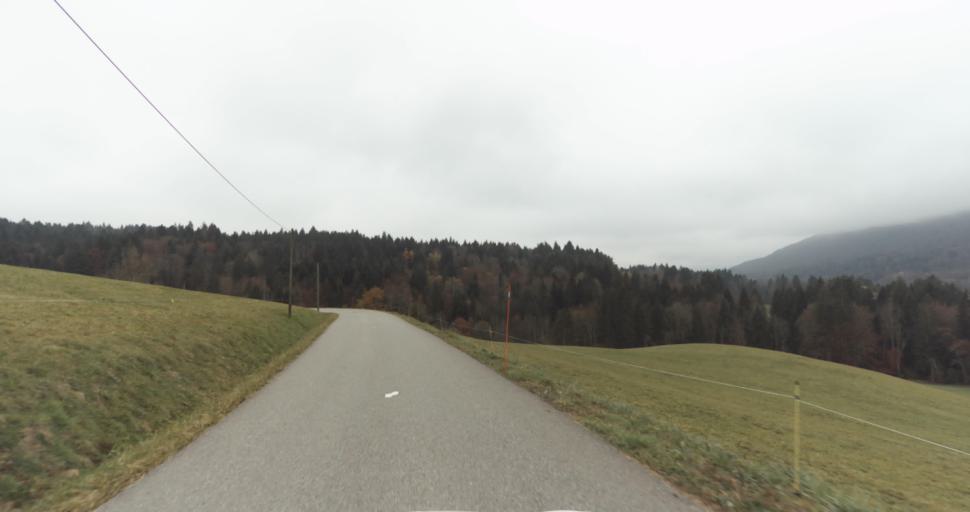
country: FR
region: Rhone-Alpes
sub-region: Departement de la Haute-Savoie
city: Saint-Jorioz
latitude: 45.7655
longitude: 6.1309
